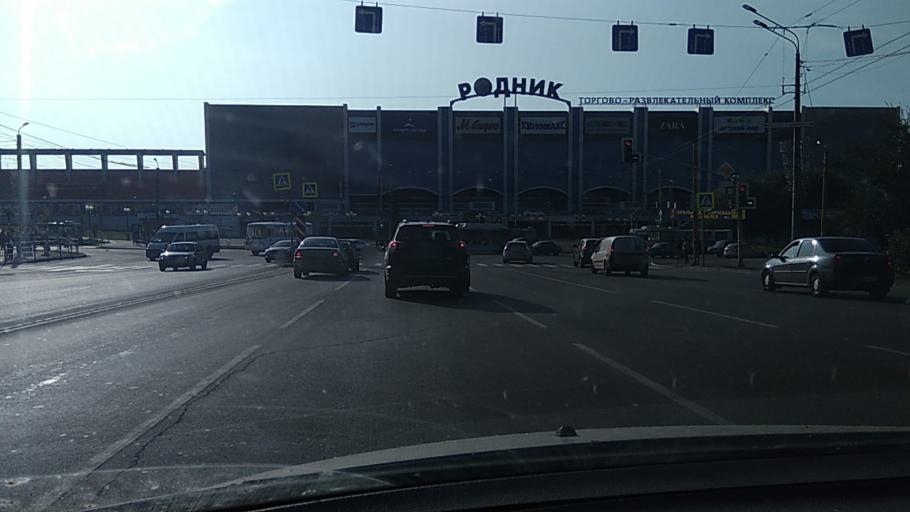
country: RU
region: Chelyabinsk
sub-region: Gorod Chelyabinsk
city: Chelyabinsk
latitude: 55.1709
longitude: 61.3596
